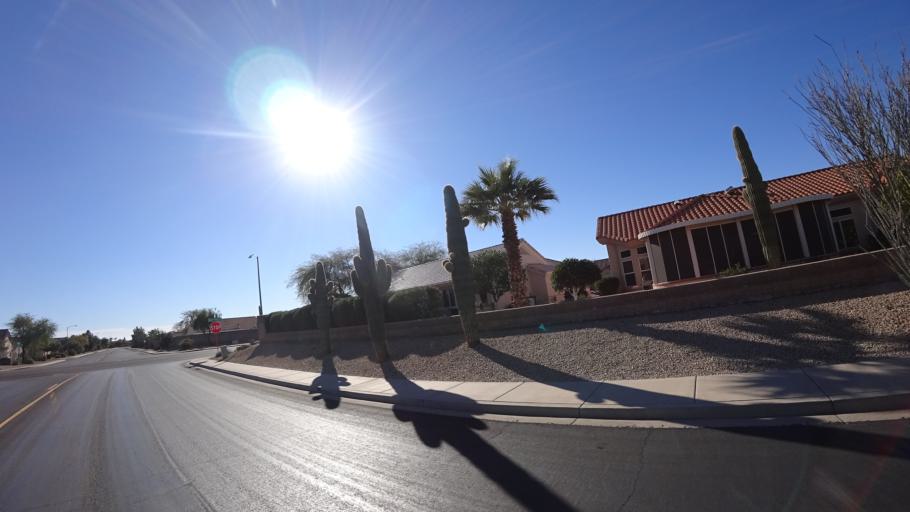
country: US
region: Arizona
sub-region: Maricopa County
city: Sun City West
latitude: 33.6883
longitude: -112.3681
